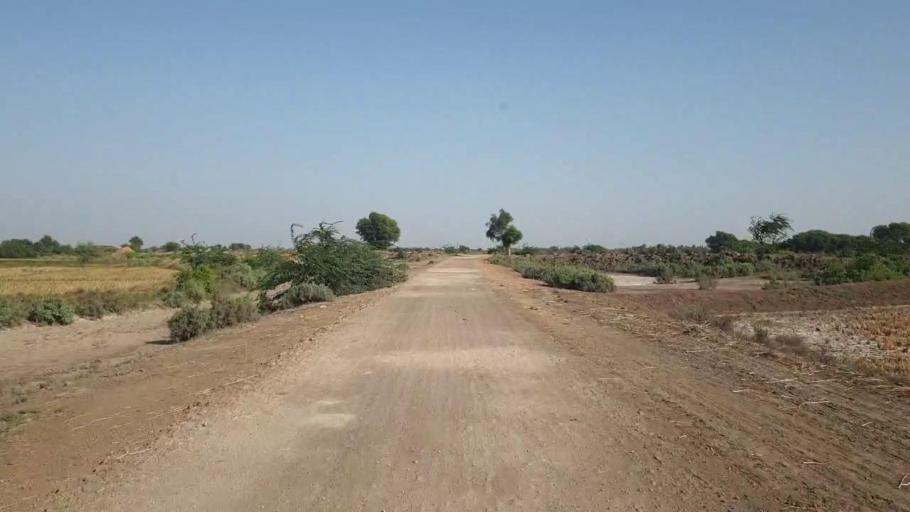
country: PK
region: Sindh
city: Rajo Khanani
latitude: 25.0086
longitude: 68.7786
